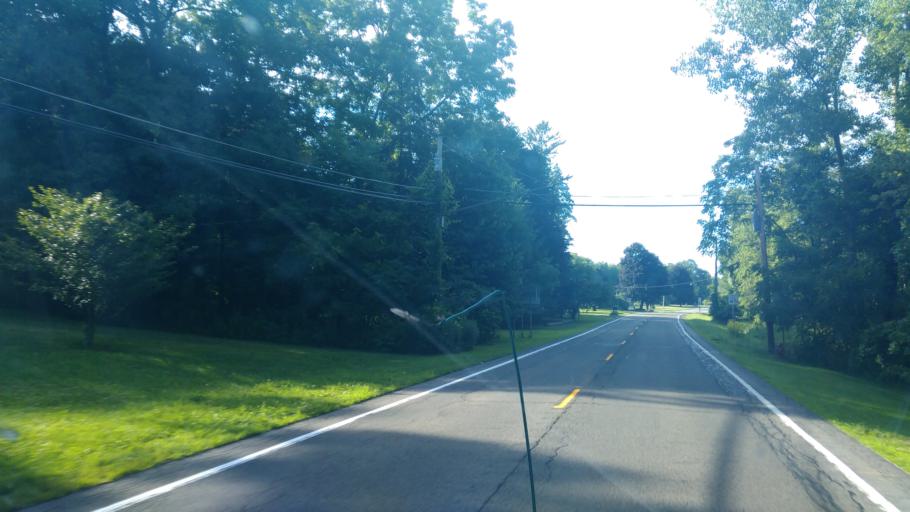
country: US
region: New York
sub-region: Wayne County
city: Lyons
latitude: 43.0766
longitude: -76.9900
